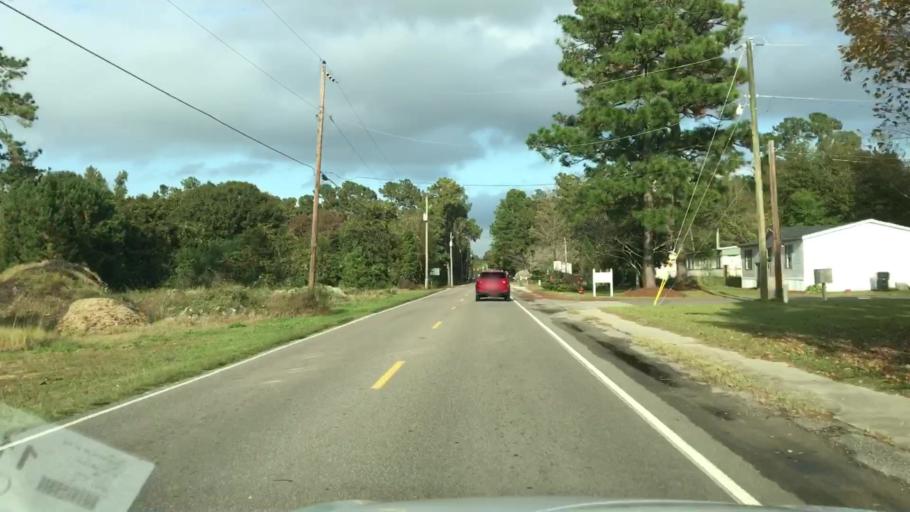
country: US
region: South Carolina
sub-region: Berkeley County
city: Sangaree
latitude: 33.0281
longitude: -80.1147
